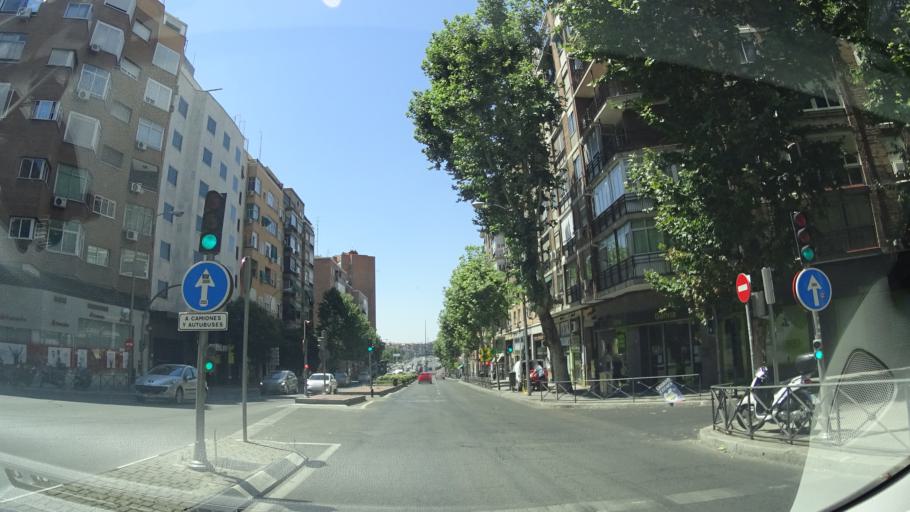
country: ES
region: Madrid
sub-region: Provincia de Madrid
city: Arganzuela
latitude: 40.3991
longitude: -3.7010
